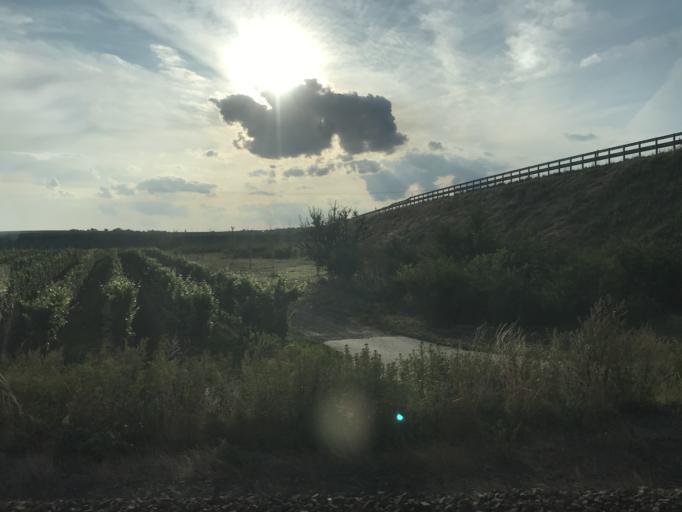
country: DE
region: Rheinland-Pfalz
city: Mettenheim
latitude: 49.7272
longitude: 8.3300
